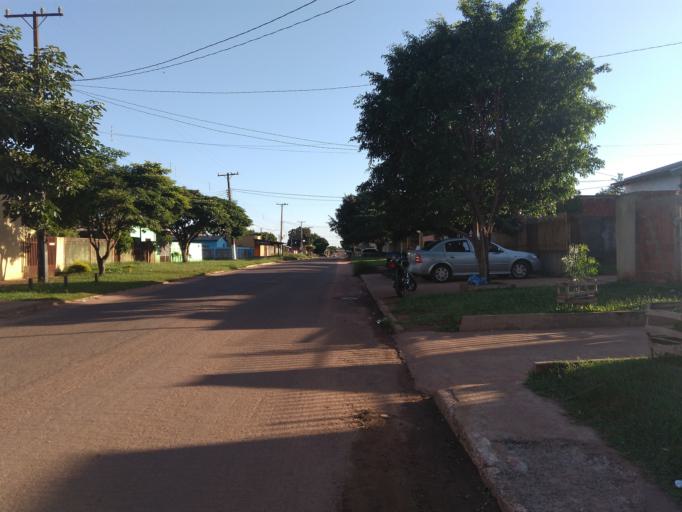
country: BR
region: Mato Grosso do Sul
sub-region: Ponta Pora
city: Ponta Pora
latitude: -22.5015
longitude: -55.7288
